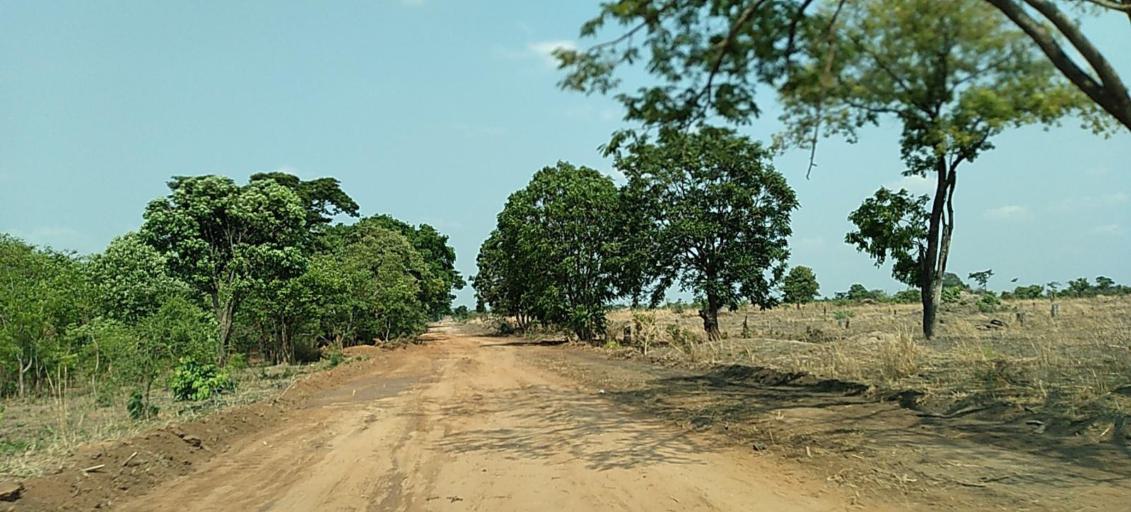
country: ZM
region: Copperbelt
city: Luanshya
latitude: -13.0901
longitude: 28.2727
